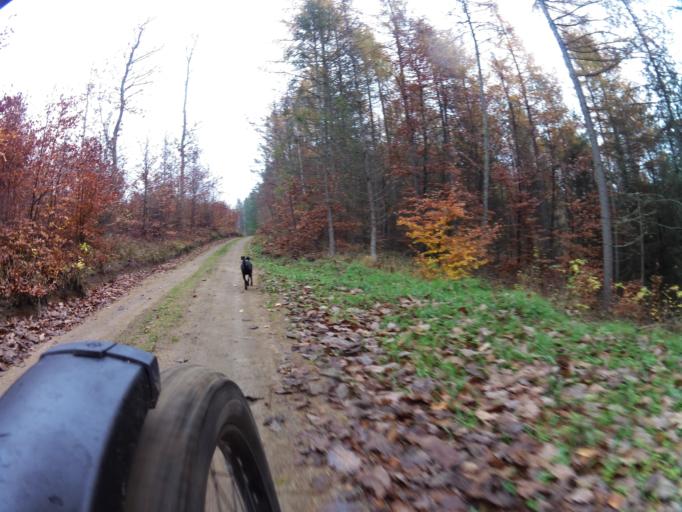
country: PL
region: Pomeranian Voivodeship
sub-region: Powiat wejherowski
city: Orle
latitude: 54.6992
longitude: 18.1551
